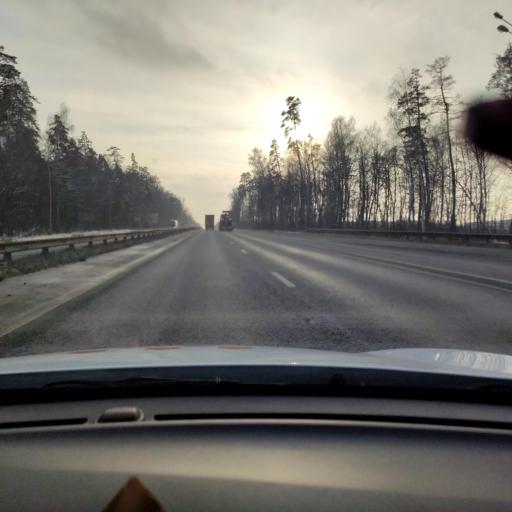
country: RU
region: Tatarstan
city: Osinovo
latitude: 55.8540
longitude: 48.8540
